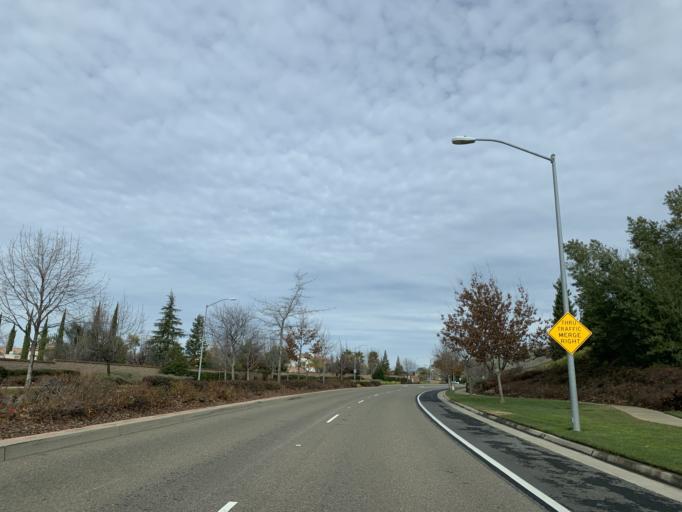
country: US
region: California
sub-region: El Dorado County
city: El Dorado Hills
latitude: 38.6700
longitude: -121.0986
